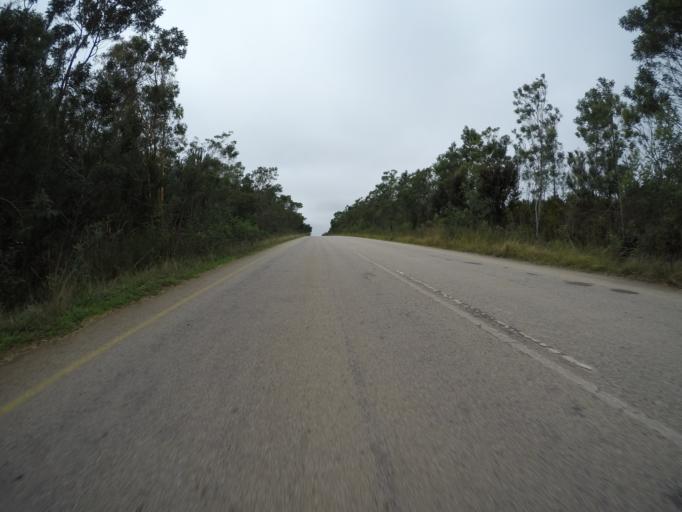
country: ZA
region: Eastern Cape
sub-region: Cacadu District Municipality
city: Kareedouw
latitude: -33.9970
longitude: 24.1619
